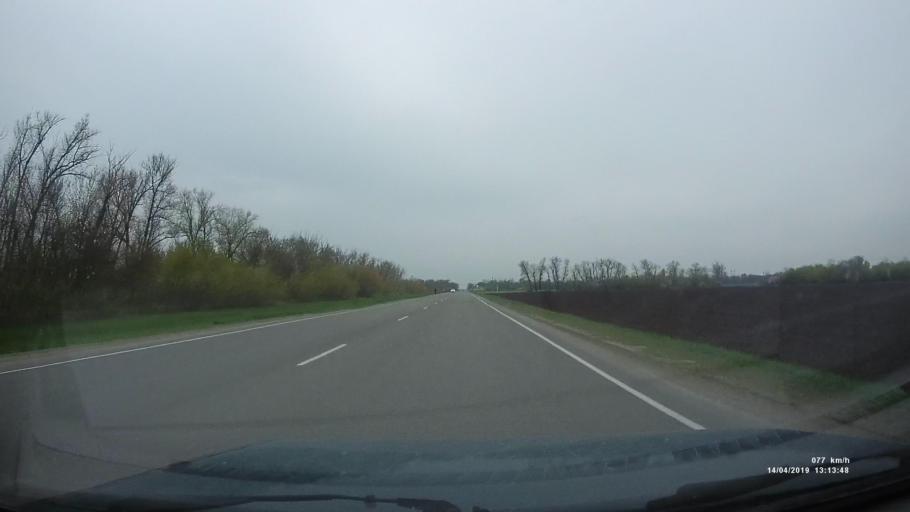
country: RU
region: Rostov
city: Kuleshovka
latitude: 47.0946
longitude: 39.6188
